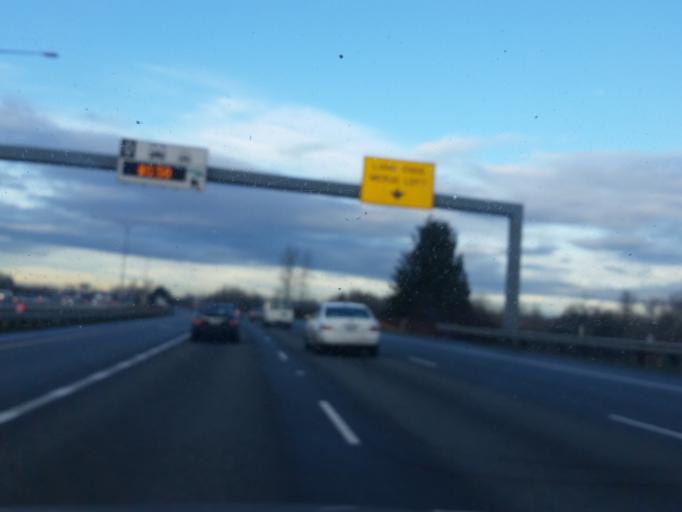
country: US
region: Washington
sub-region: King County
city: Auburn
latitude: 47.3124
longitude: -122.2460
